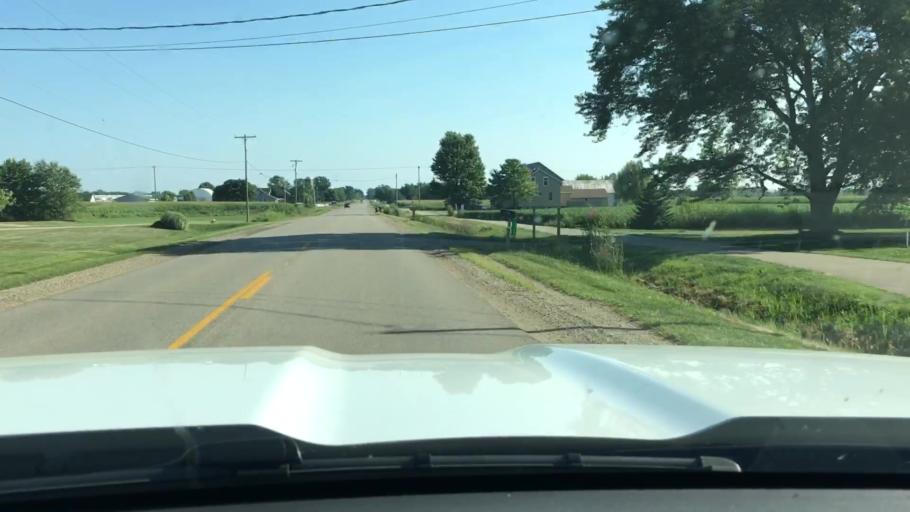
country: US
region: Michigan
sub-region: Ottawa County
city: Zeeland
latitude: 42.7996
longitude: -85.9401
